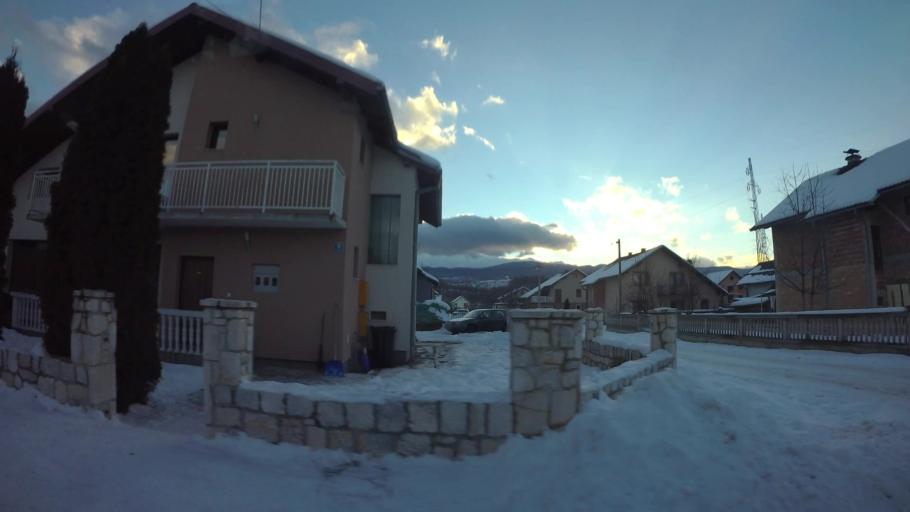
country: BA
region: Federation of Bosnia and Herzegovina
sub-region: Kanton Sarajevo
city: Sarajevo
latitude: 43.8083
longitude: 18.3726
